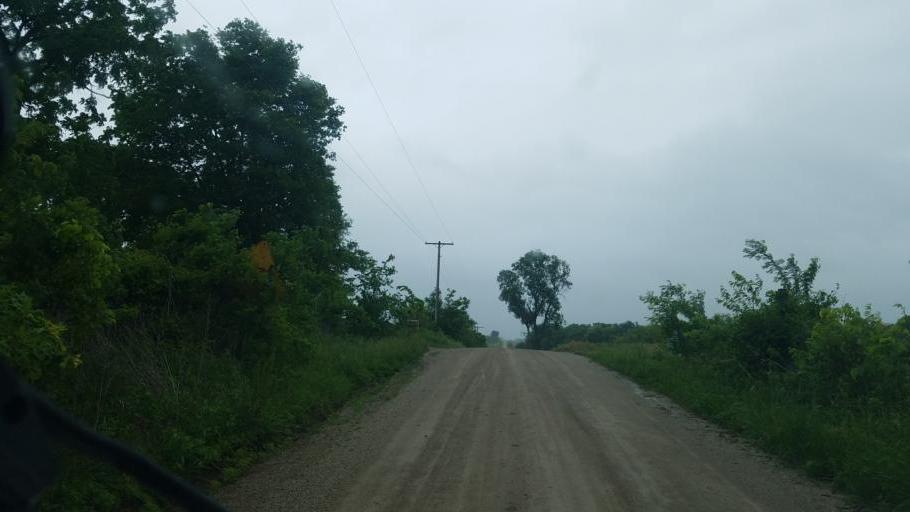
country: US
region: Missouri
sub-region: Carroll County
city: Carrollton
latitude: 39.4707
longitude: -93.4738
